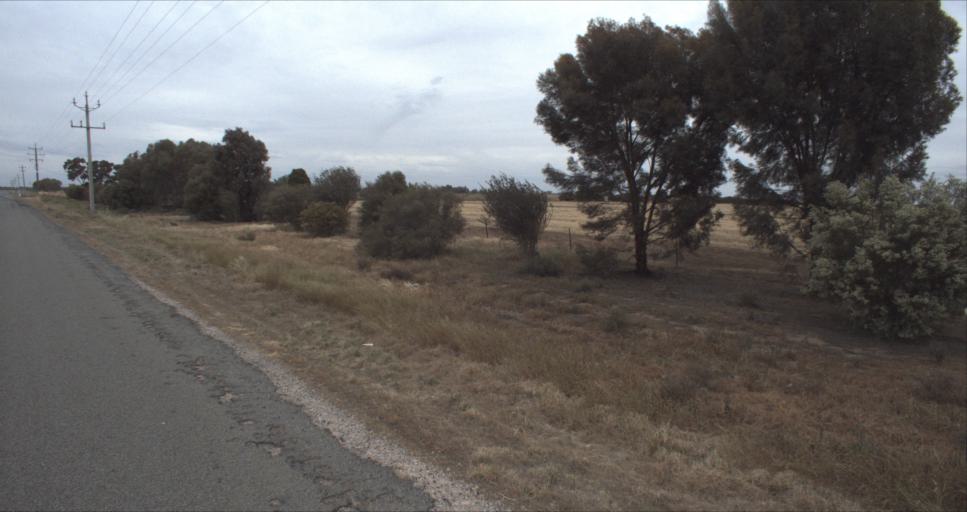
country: AU
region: New South Wales
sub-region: Leeton
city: Leeton
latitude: -34.4932
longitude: 146.4011
